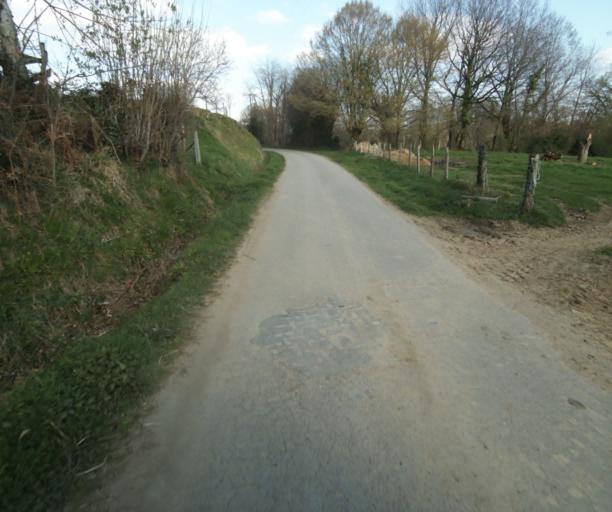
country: FR
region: Limousin
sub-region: Departement de la Correze
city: Saint-Mexant
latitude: 45.3383
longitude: 1.5960
